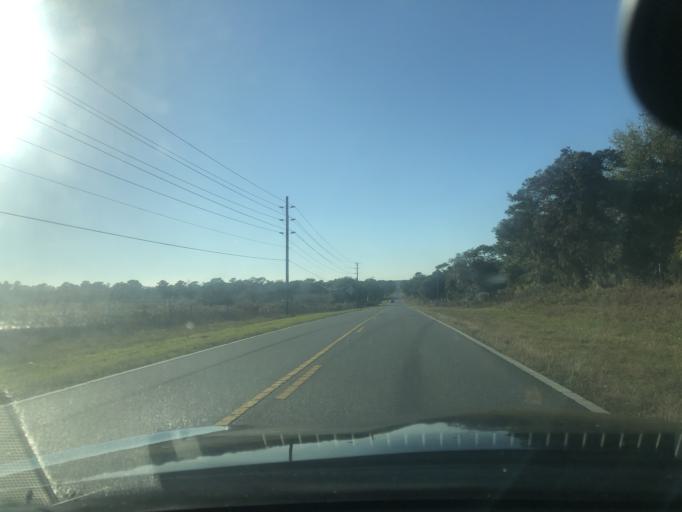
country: US
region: Florida
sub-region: Citrus County
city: Sugarmill Woods
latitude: 28.7641
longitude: -82.5225
